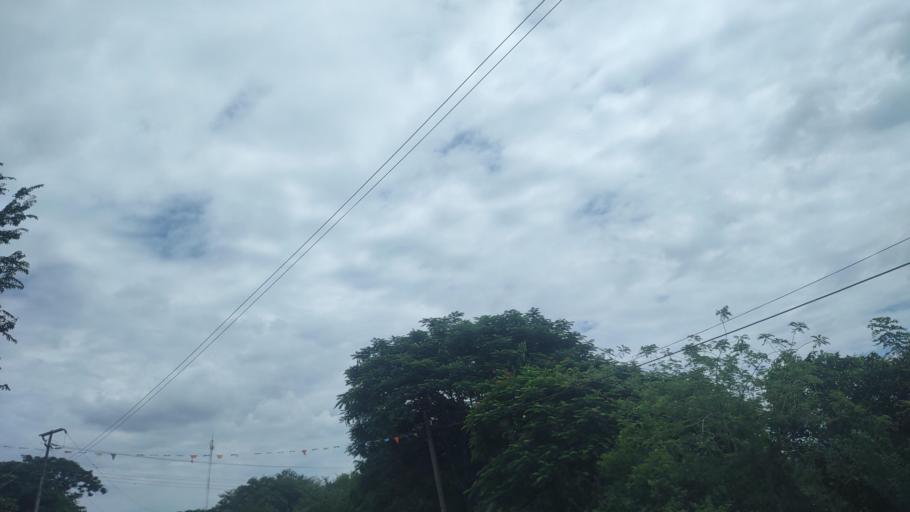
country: MX
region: Veracruz
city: Chicontepec de Tejada
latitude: 21.0485
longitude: -98.0014
